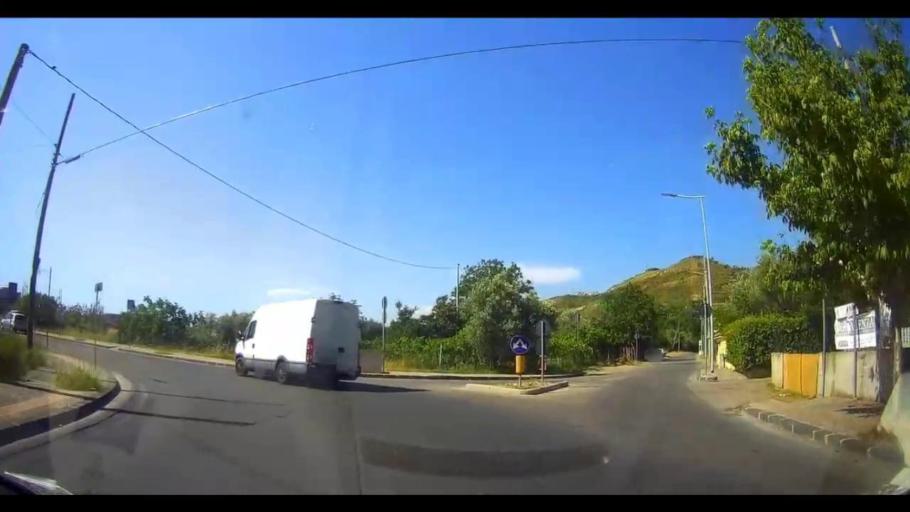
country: IT
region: Calabria
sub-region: Provincia di Cosenza
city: Cosenza
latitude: 39.3000
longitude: 16.2632
